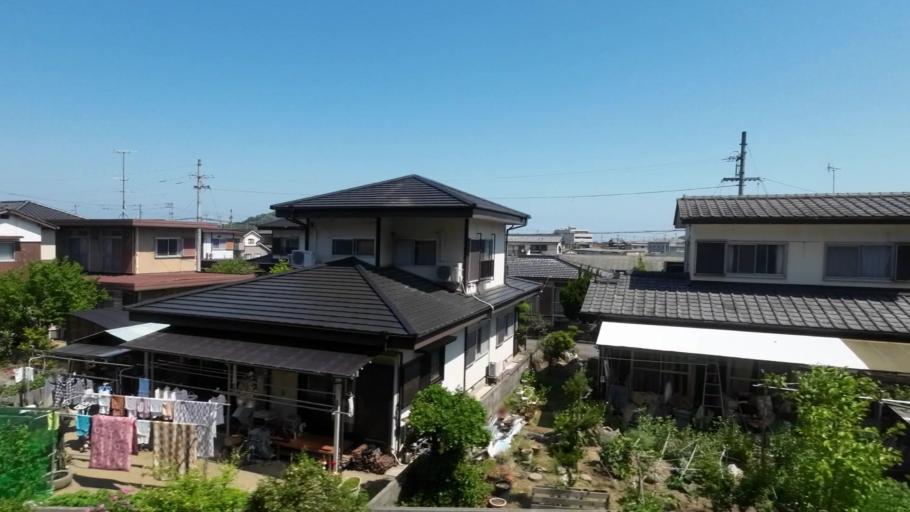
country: JP
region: Ehime
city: Niihama
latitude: 33.9704
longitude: 133.3300
